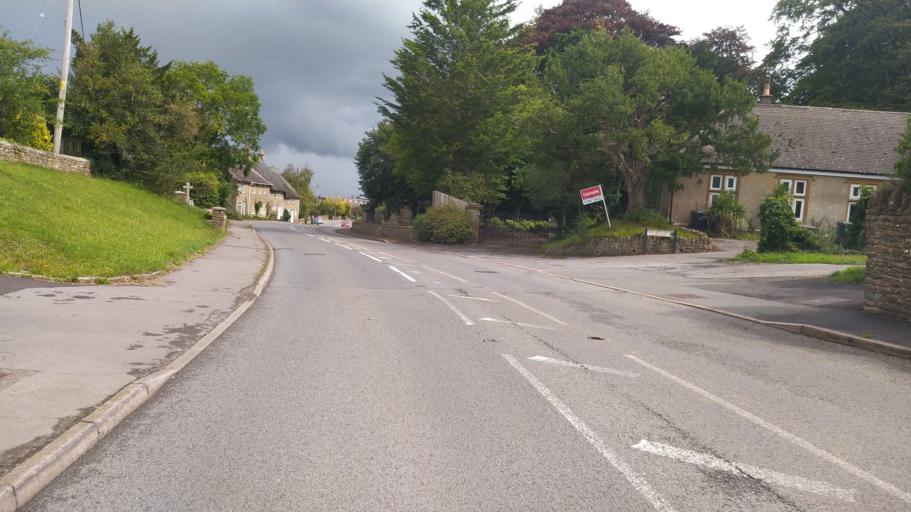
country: GB
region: England
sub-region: Somerset
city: Milborne Port
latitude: 50.9166
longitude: -2.4347
